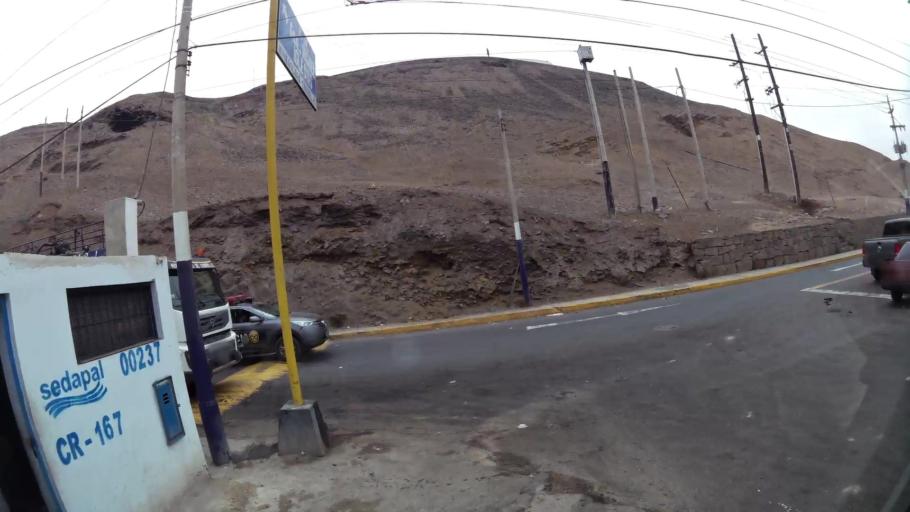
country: PE
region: Lima
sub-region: Lima
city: Surco
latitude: -12.1724
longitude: -77.0288
